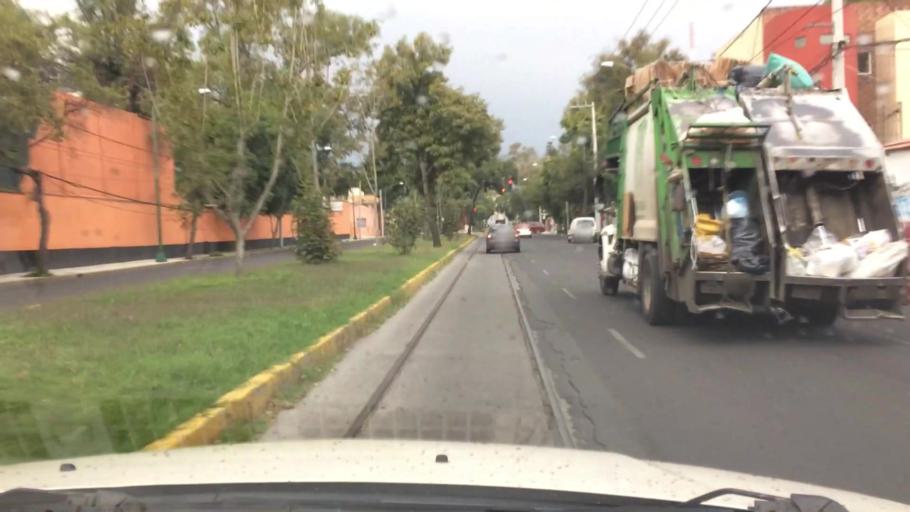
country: MX
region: Mexico City
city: Tlalpan
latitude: 19.2942
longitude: -99.1631
